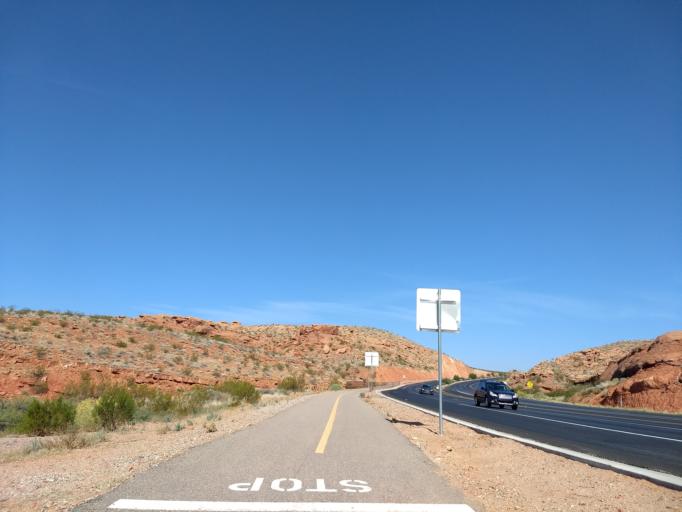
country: US
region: Utah
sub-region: Washington County
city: Saint George
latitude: 37.1178
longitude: -113.5821
